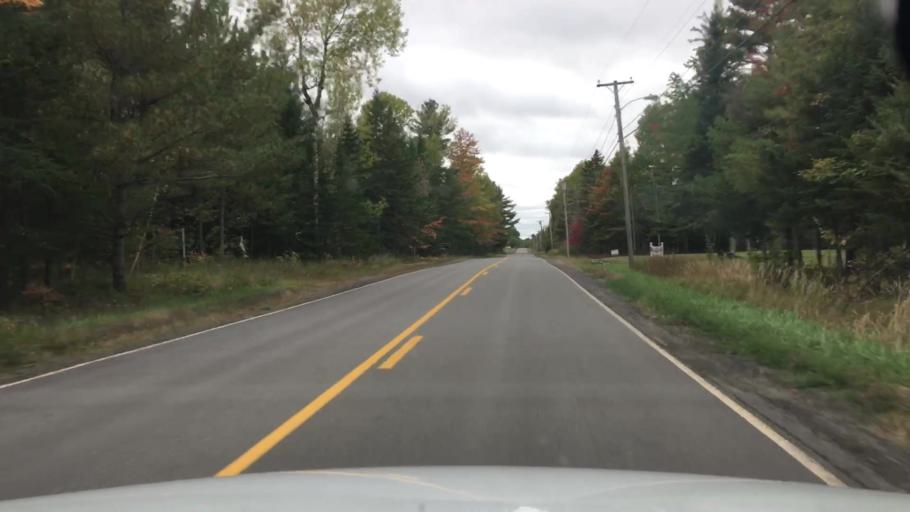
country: US
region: Maine
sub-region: Penobscot County
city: Hudson
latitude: 44.9887
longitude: -68.7592
